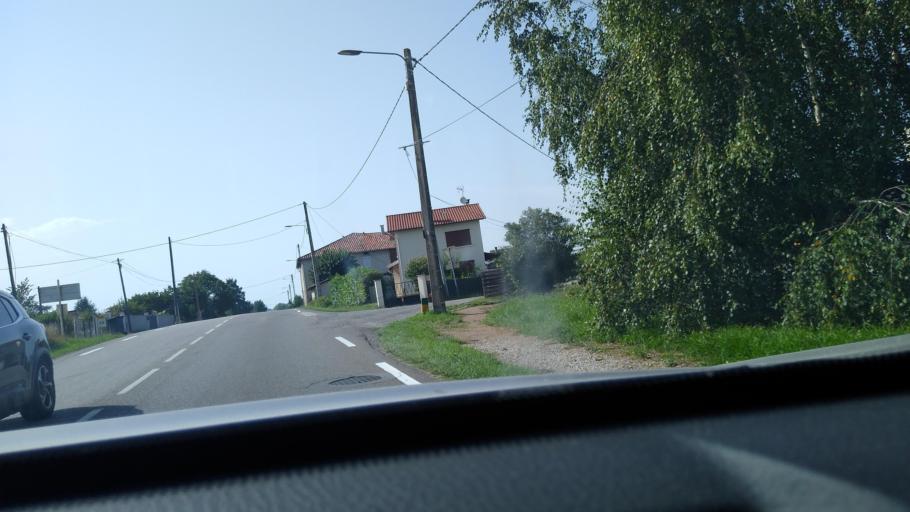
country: FR
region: Midi-Pyrenees
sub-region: Departement de l'Ariege
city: Saint-Lizier
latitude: 43.0110
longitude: 1.1164
